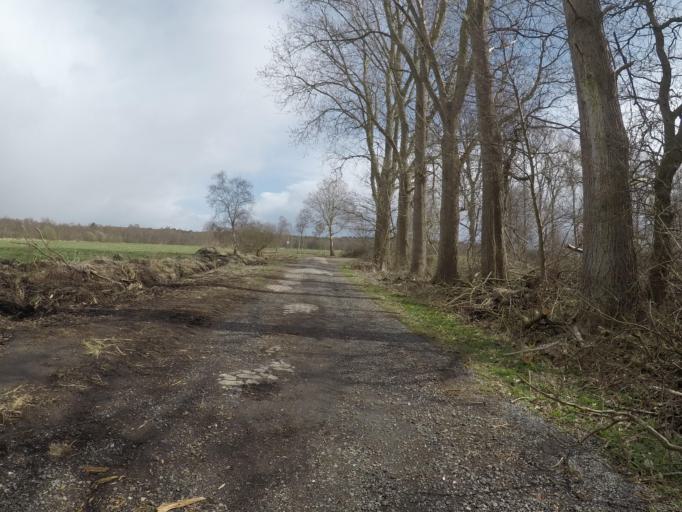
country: DE
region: Lower Saxony
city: Elmlohe
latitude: 53.6034
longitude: 8.7129
